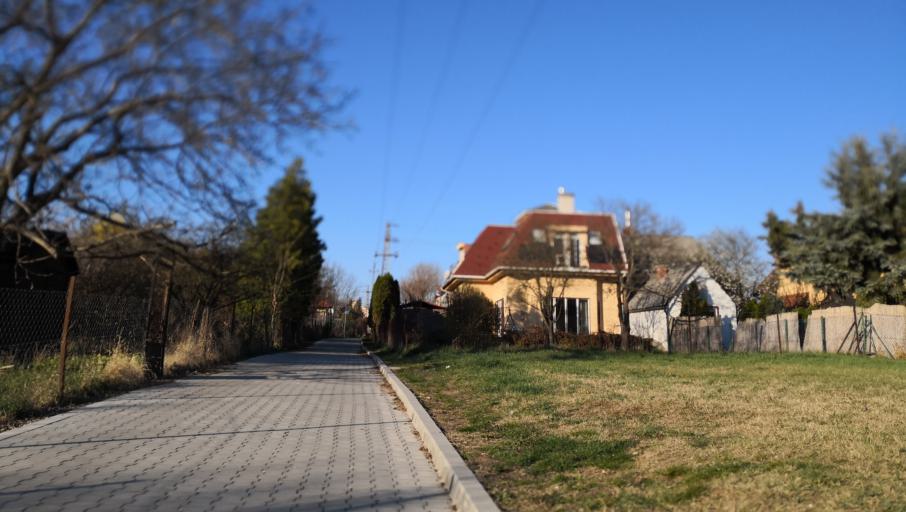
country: HU
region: Pest
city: Csomor
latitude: 47.5160
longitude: 19.2308
